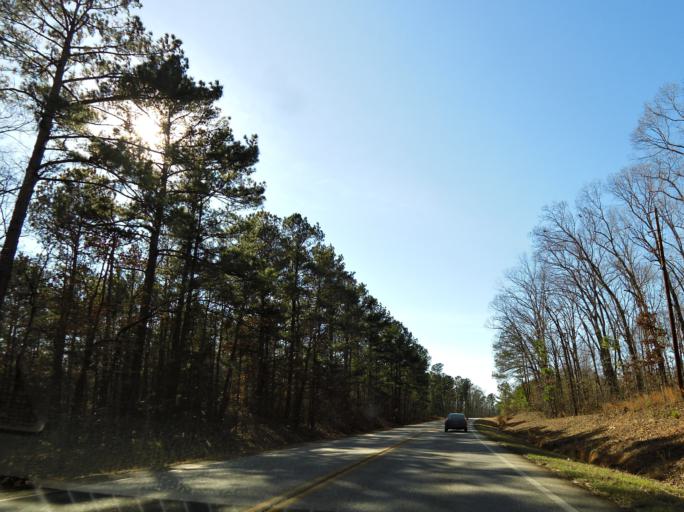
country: US
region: Georgia
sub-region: Crawford County
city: Roberta
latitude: 32.8735
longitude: -84.0347
